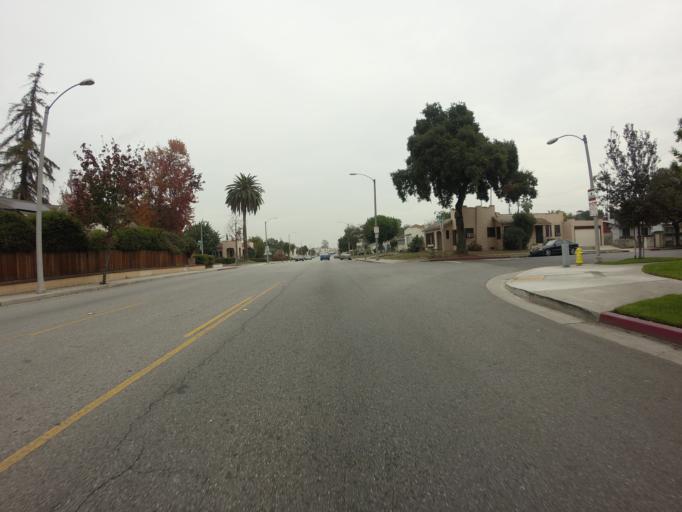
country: US
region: California
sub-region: Los Angeles County
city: Alhambra
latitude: 34.0987
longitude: -118.1373
